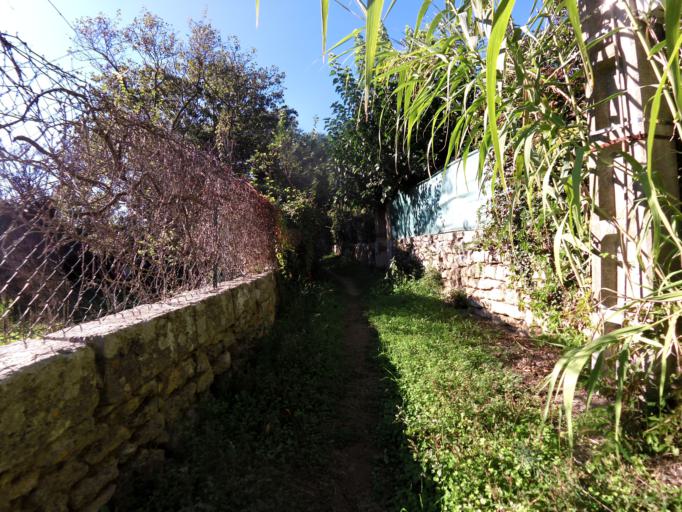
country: FR
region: Languedoc-Roussillon
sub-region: Departement du Gard
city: Aigues-Vives
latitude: 43.7397
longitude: 4.1685
